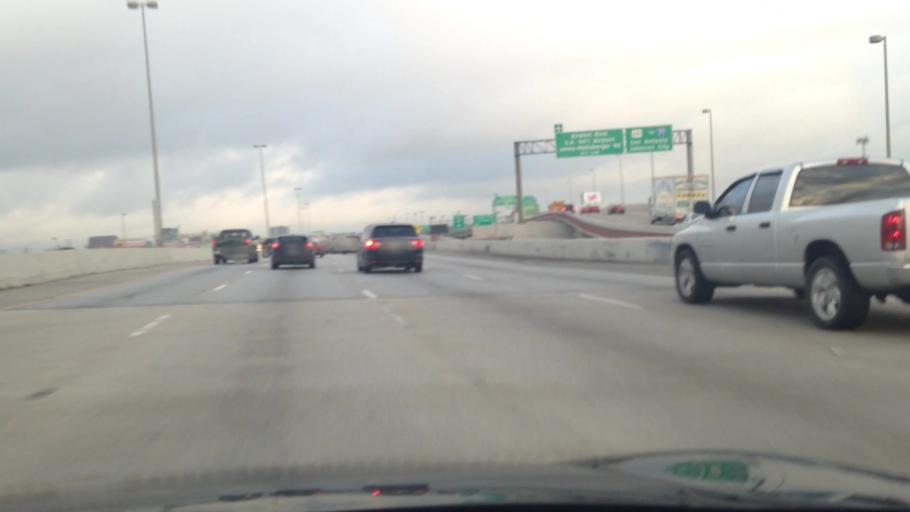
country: US
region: Texas
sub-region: Bexar County
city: Alamo Heights
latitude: 29.5171
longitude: -98.4646
